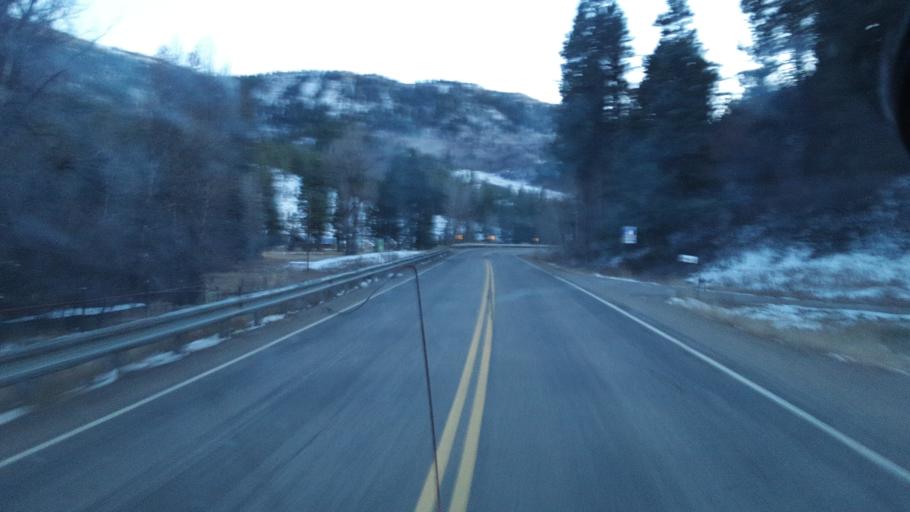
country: US
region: Colorado
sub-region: La Plata County
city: Durango
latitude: 37.3360
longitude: -107.7249
